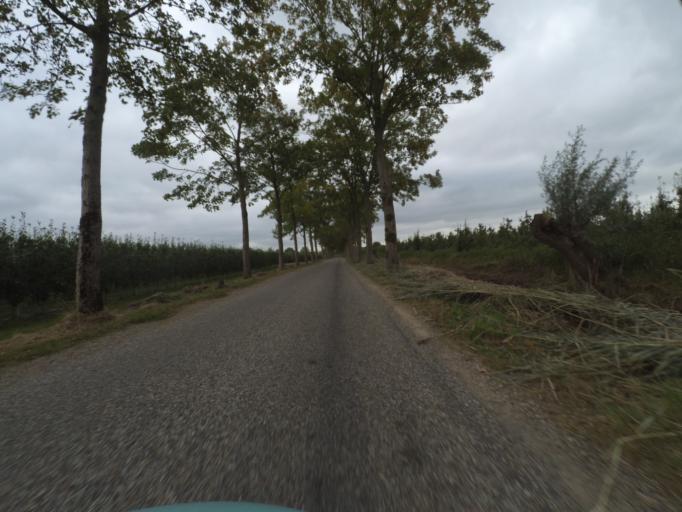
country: NL
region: Gelderland
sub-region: Gemeente Buren
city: Lienden
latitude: 51.9594
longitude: 5.5083
